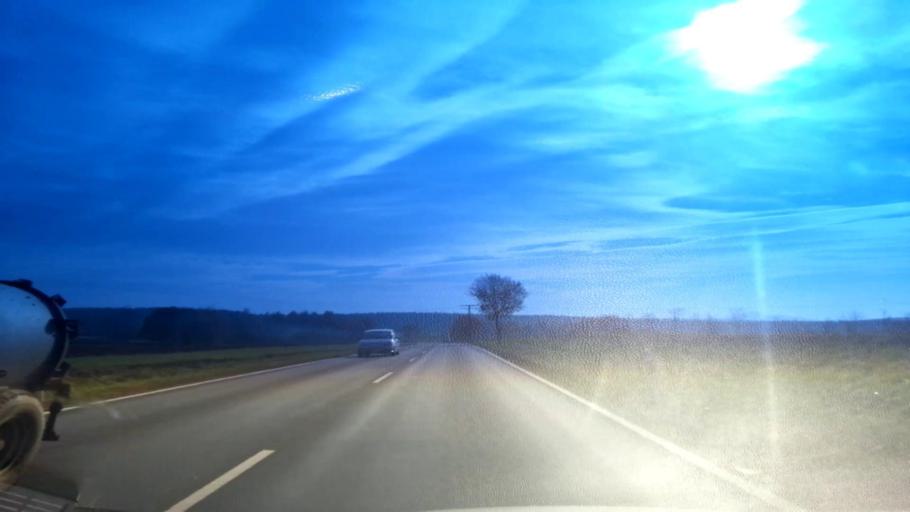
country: DE
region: Bavaria
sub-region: Upper Franconia
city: Kirchenpingarten
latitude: 49.9187
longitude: 11.8212
